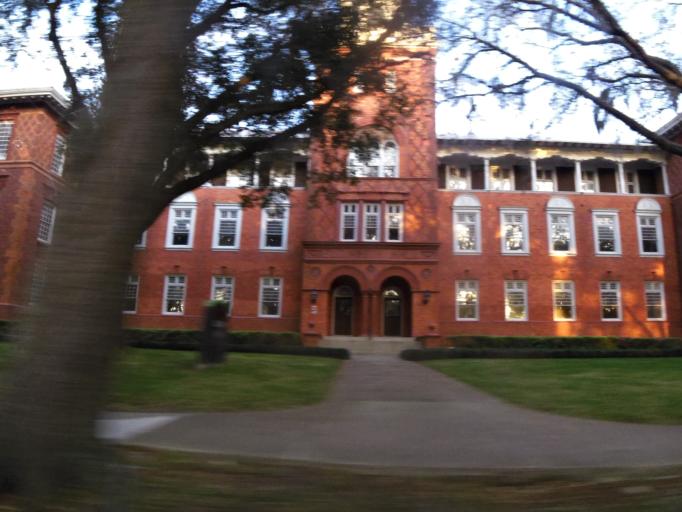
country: US
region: Florida
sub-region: Volusia County
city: DeLand
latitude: 29.0349
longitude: -81.3036
